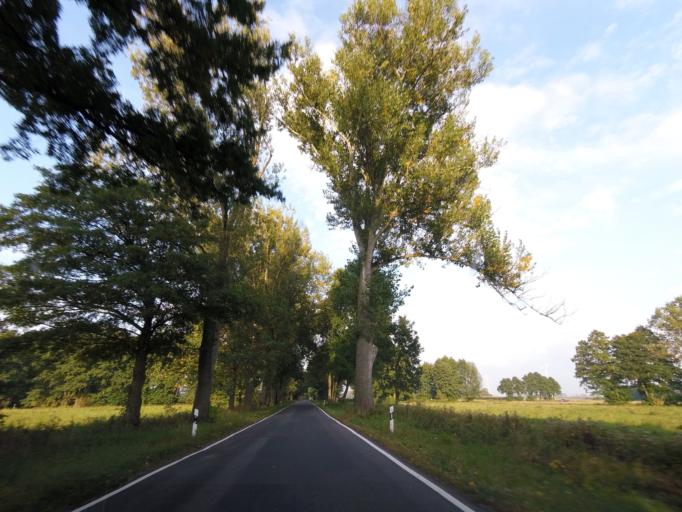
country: DE
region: Brandenburg
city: Linthe
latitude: 52.1593
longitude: 12.7969
